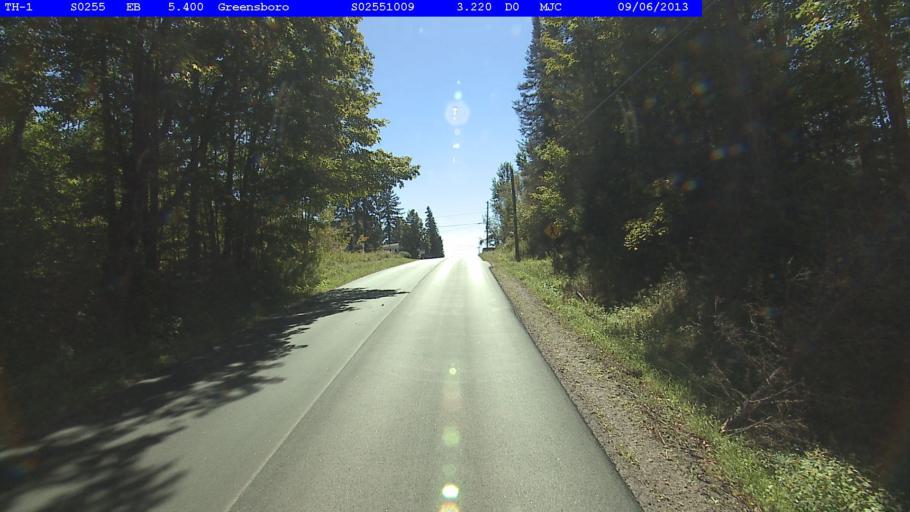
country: US
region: Vermont
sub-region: Caledonia County
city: Hardwick
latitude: 44.6012
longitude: -72.3064
